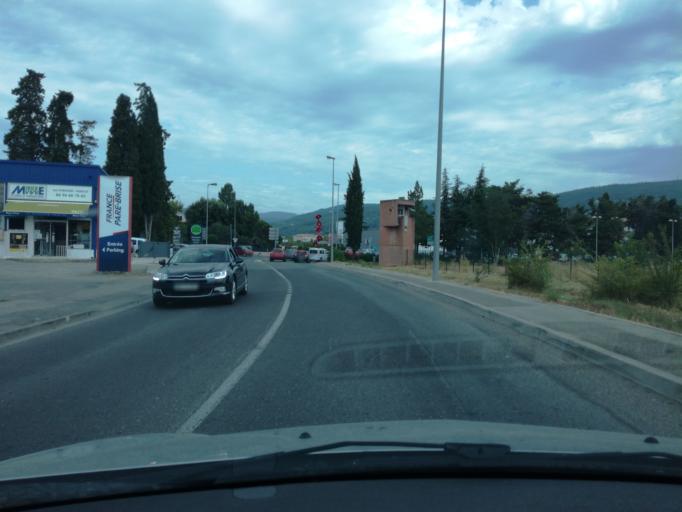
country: FR
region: Provence-Alpes-Cote d'Azur
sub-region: Departement du Var
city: Draguignan
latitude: 43.5310
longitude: 6.4498
